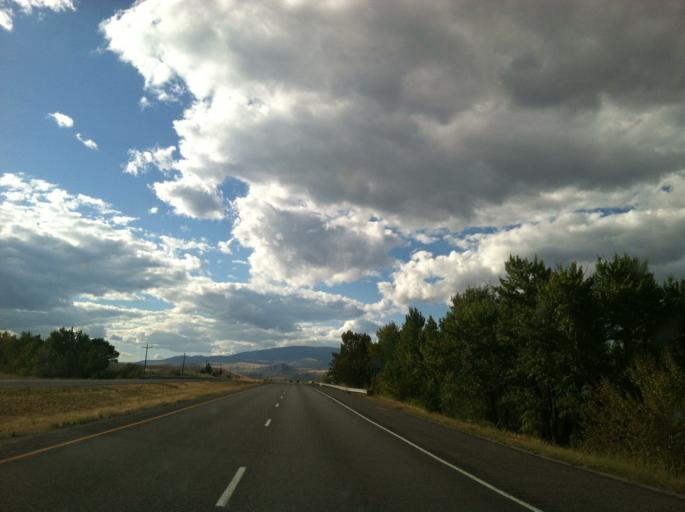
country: US
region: Montana
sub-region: Deer Lodge County
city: Anaconda
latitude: 46.1085
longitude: -112.8517
